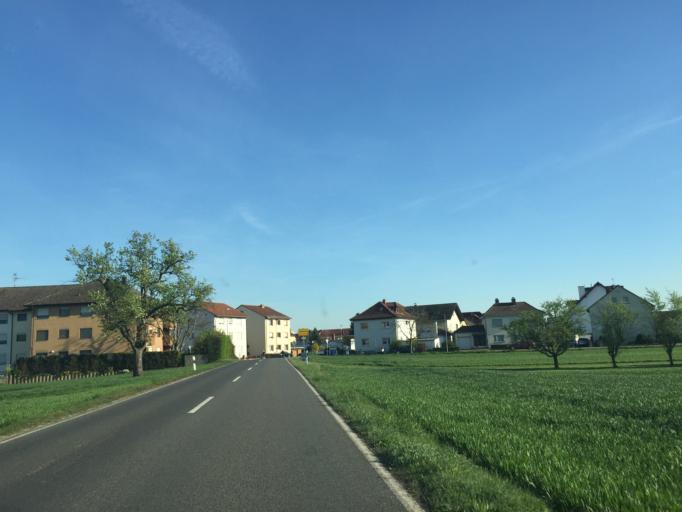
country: DE
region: Baden-Wuerttemberg
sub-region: Karlsruhe Region
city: Heddesheim
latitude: 49.5102
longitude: 8.5977
